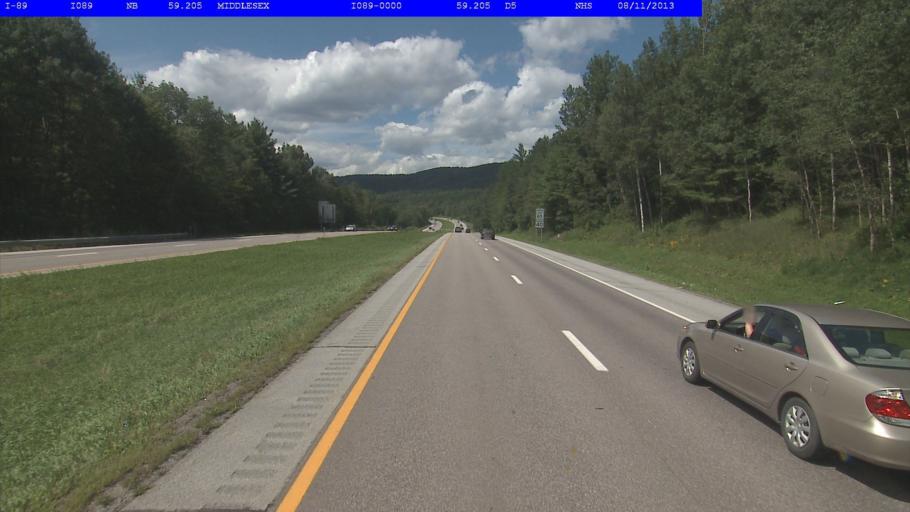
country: US
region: Vermont
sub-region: Washington County
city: Waterbury
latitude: 44.3043
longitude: -72.6900
